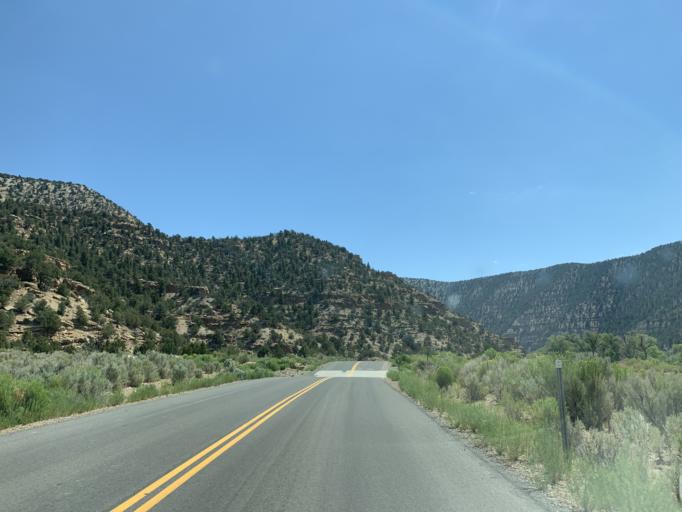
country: US
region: Utah
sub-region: Carbon County
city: East Carbon City
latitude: 39.7869
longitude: -110.4152
